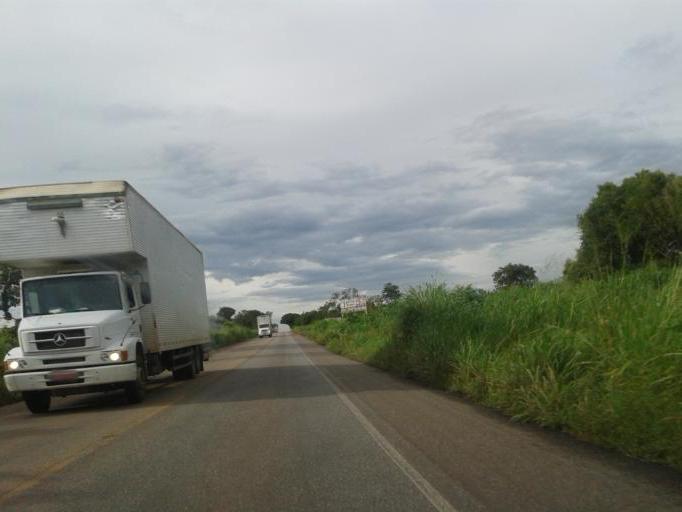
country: BR
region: Goias
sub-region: Mozarlandia
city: Mozarlandia
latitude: -14.7691
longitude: -50.5373
